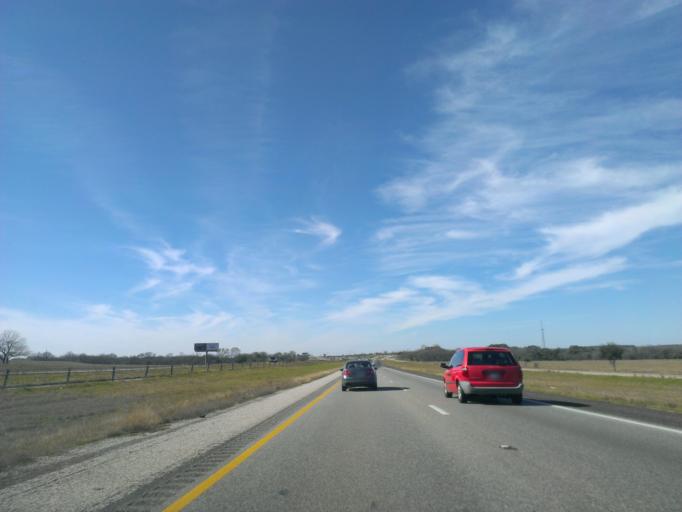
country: US
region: Texas
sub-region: Bell County
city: Nolanville
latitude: 31.0641
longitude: -97.5720
